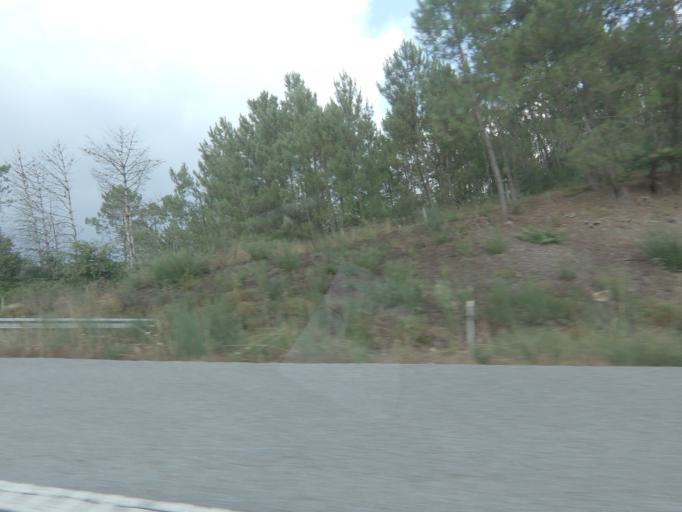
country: PT
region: Viseu
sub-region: Castro Daire
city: Castro Daire
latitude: 40.9113
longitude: -7.9072
